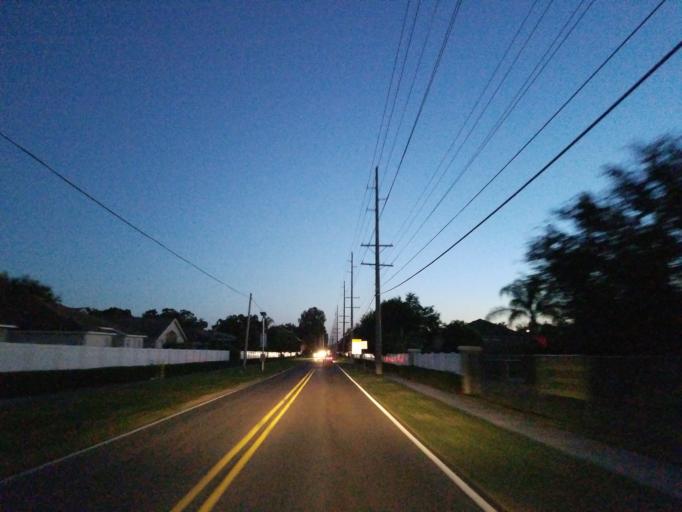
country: US
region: Florida
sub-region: Hillsborough County
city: Bloomingdale
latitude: 27.9053
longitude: -82.2278
